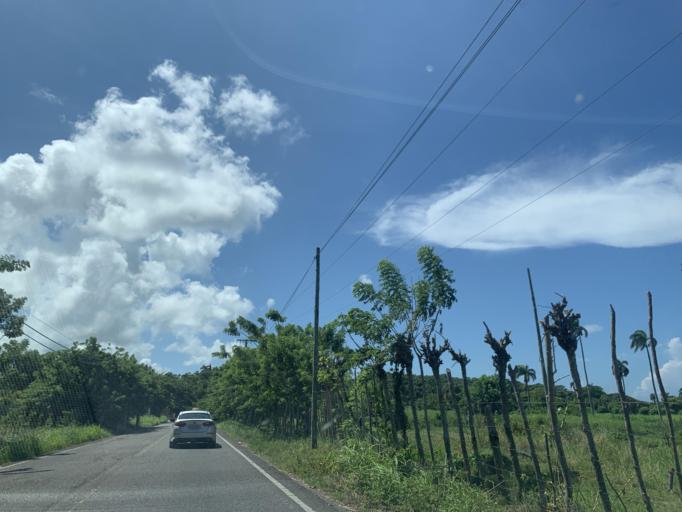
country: DO
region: Maria Trinidad Sanchez
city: Cabrera
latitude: 19.6483
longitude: -69.9255
